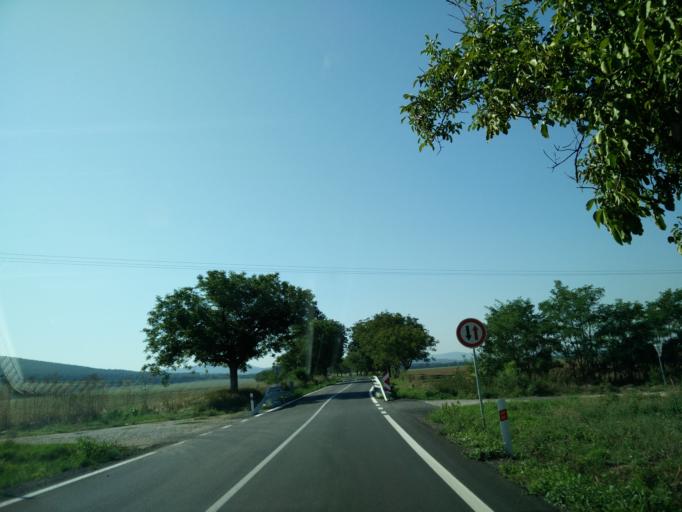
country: SK
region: Nitriansky
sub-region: Okres Nitra
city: Nitra
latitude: 48.4594
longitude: 18.1432
